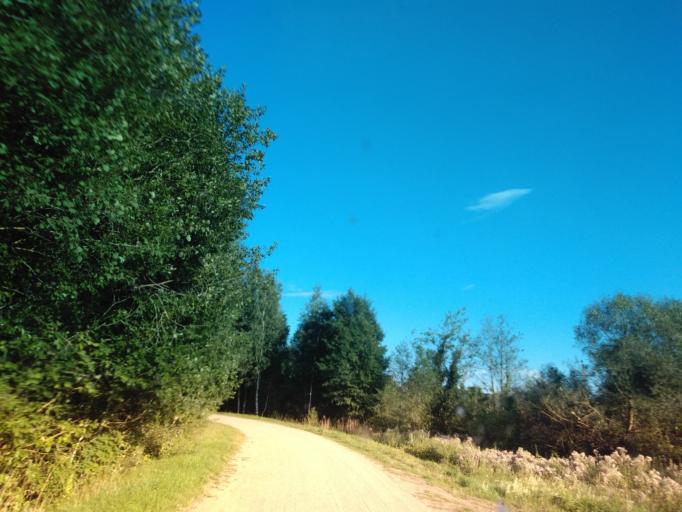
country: BY
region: Minsk
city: Uzda
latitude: 53.3456
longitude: 27.0922
